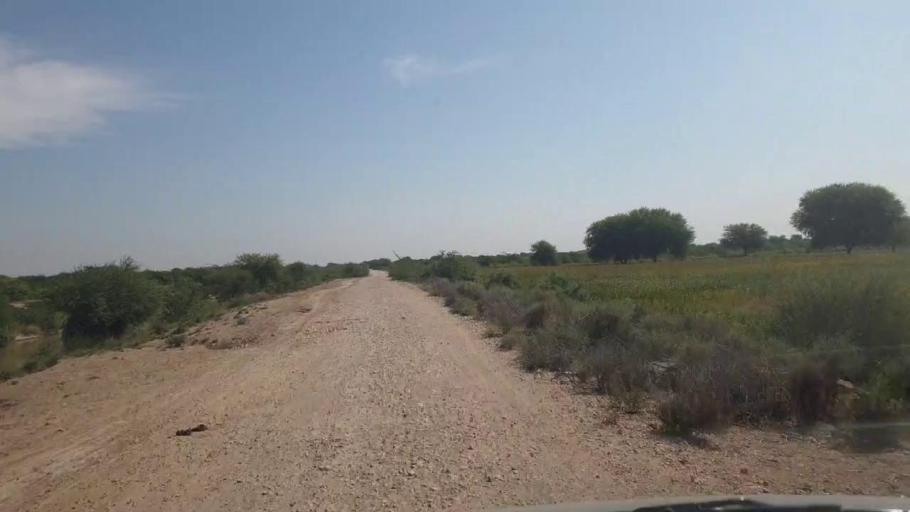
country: PK
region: Sindh
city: Digri
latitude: 24.9551
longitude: 69.1395
